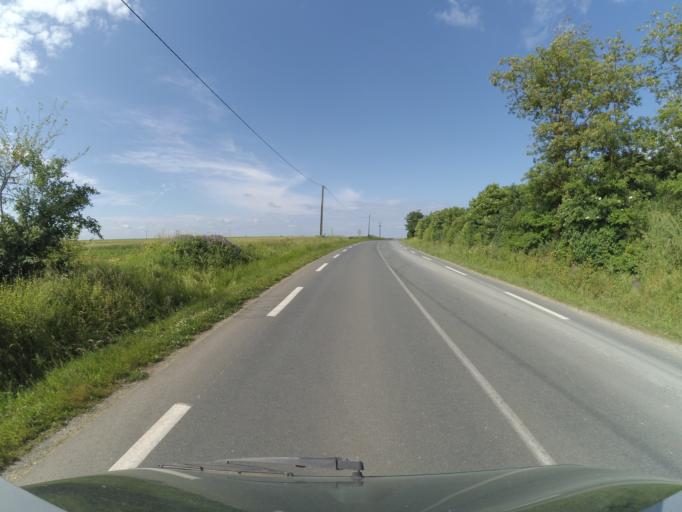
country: FR
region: Poitou-Charentes
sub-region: Departement de la Charente-Maritime
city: Saint-Xandre
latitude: 46.2234
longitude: -1.0848
